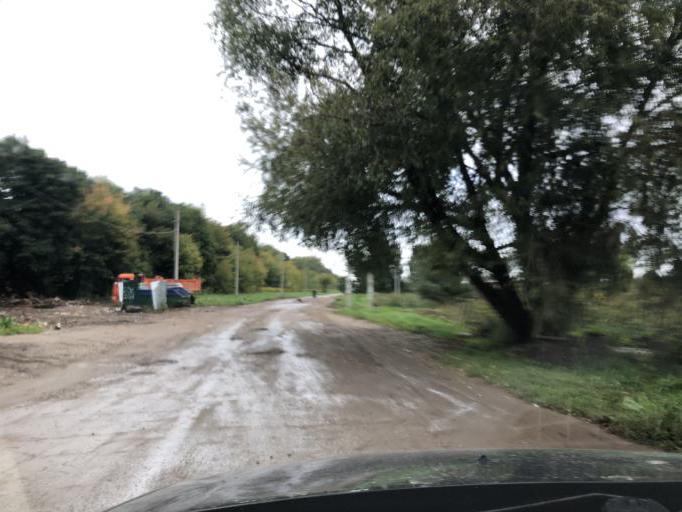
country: RU
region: Tula
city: Mendeleyevskiy
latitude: 54.1743
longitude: 37.5519
